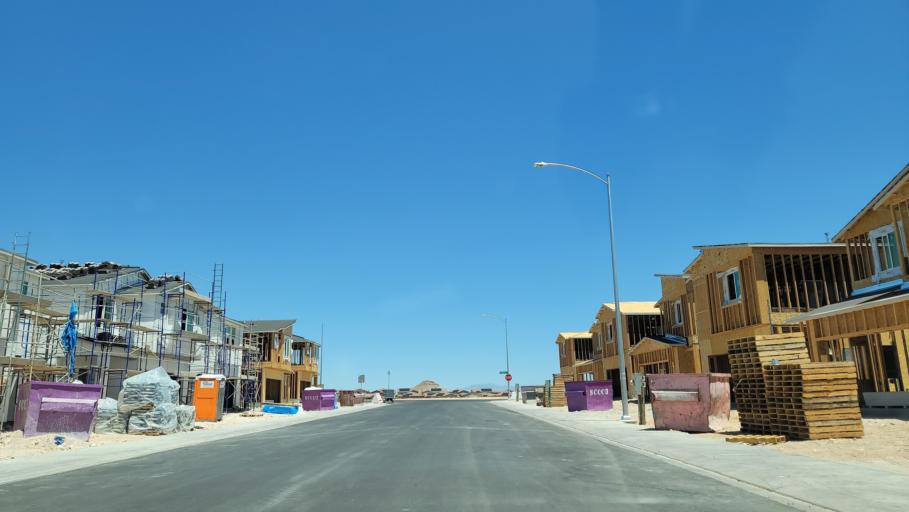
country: US
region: Nevada
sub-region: Clark County
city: Enterprise
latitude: 36.0254
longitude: -115.3016
